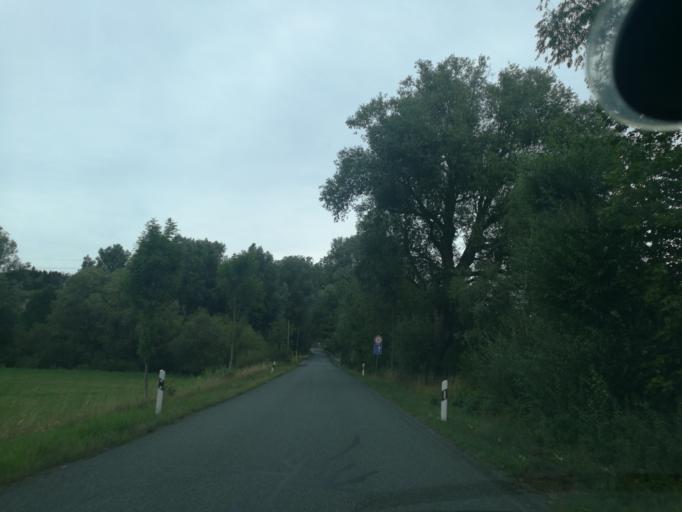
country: DE
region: Bavaria
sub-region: Upper Franconia
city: Dohlau
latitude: 50.2942
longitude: 11.9461
